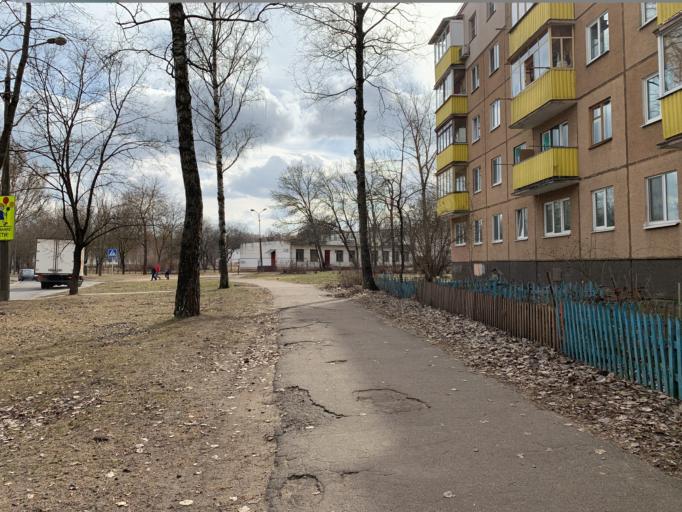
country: BY
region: Minsk
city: Borovlyany
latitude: 53.9507
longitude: 27.6295
